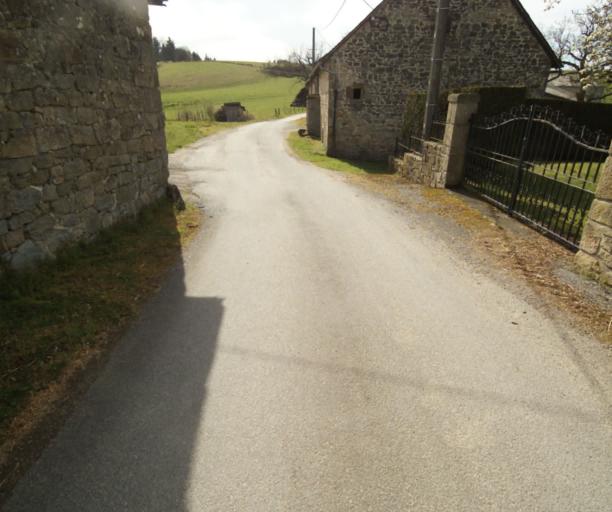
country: FR
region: Limousin
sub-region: Departement de la Correze
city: Correze
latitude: 45.3546
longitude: 1.8650
